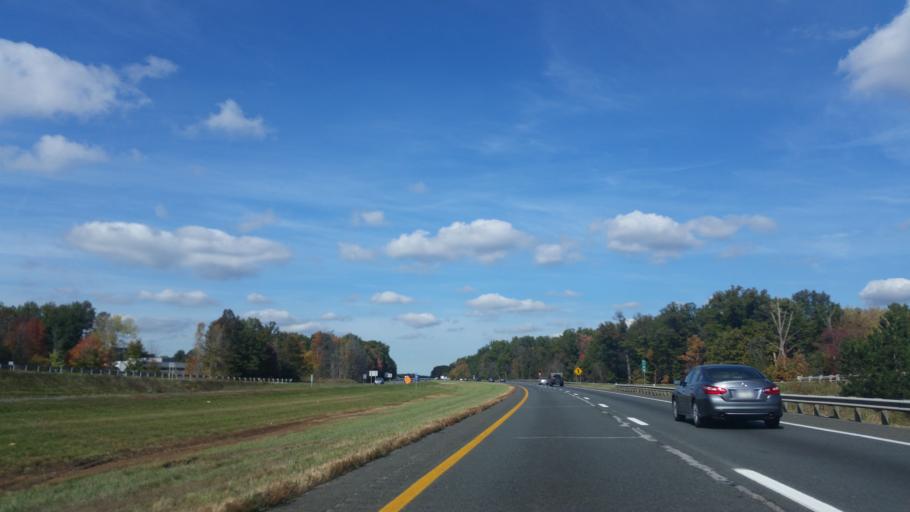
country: US
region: Ohio
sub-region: Cuyahoga County
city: Brecksville
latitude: 41.2900
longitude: -81.6368
